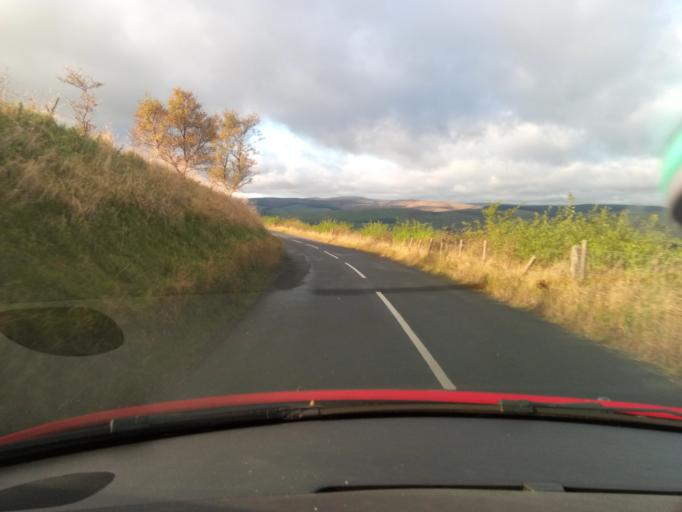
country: GB
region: Scotland
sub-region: The Scottish Borders
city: Lauder
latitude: 55.6998
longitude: -2.8337
